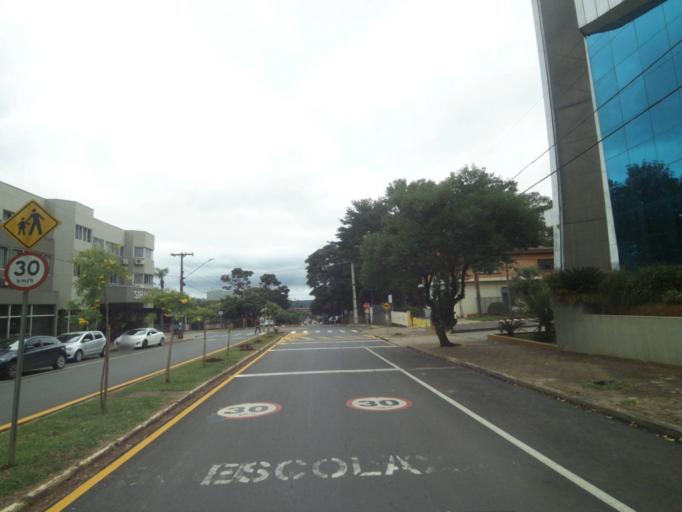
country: BR
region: Parana
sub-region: Telemaco Borba
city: Telemaco Borba
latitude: -24.3296
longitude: -50.6206
